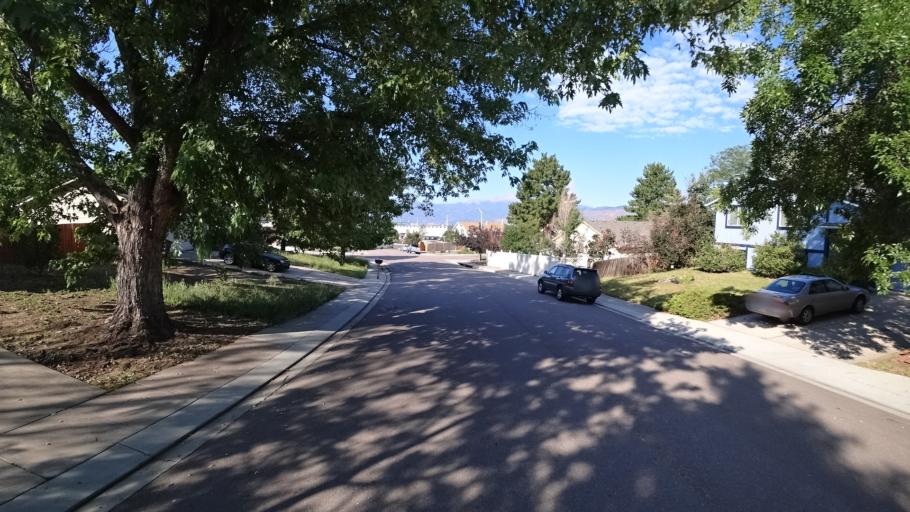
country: US
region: Colorado
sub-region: El Paso County
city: Air Force Academy
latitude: 38.9441
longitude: -104.7803
